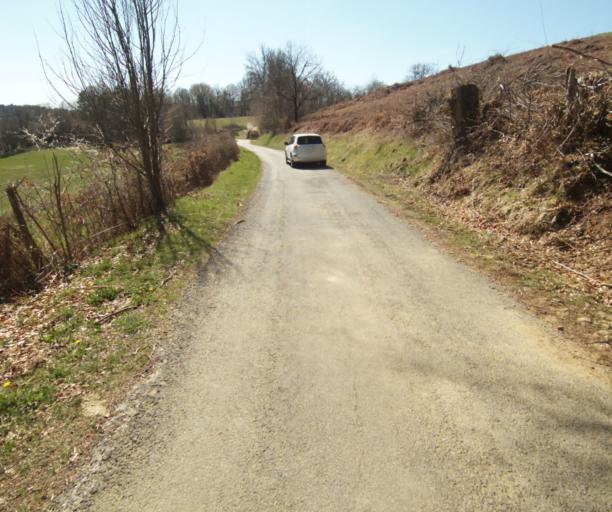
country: FR
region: Limousin
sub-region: Departement de la Correze
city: Saint-Clement
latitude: 45.3211
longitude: 1.7030
